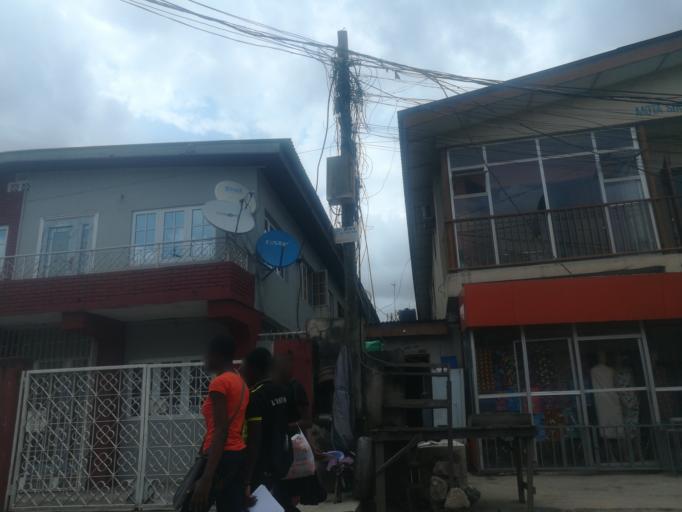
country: NG
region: Lagos
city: Ojota
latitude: 6.5621
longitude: 3.3919
